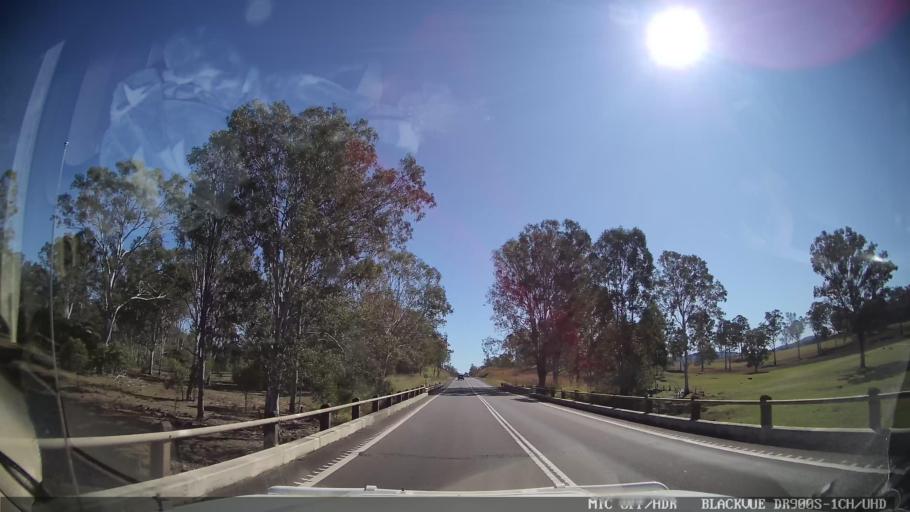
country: AU
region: Queensland
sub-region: Gympie Regional Council
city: Gympie
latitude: -26.0394
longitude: 152.5701
